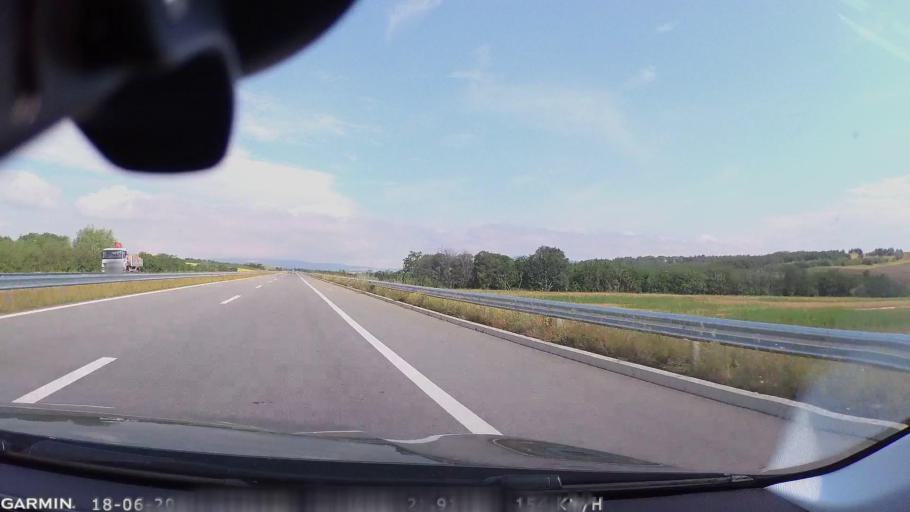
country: MK
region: Sveti Nikole
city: Gorobinci
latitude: 41.9040
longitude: 21.9107
